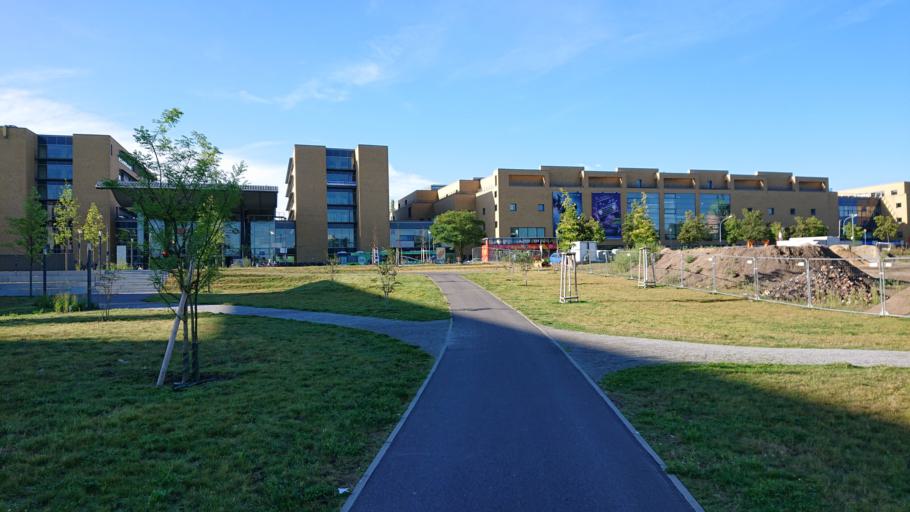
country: DE
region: Brandenburg
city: Potsdam
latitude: 52.3936
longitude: 13.0668
